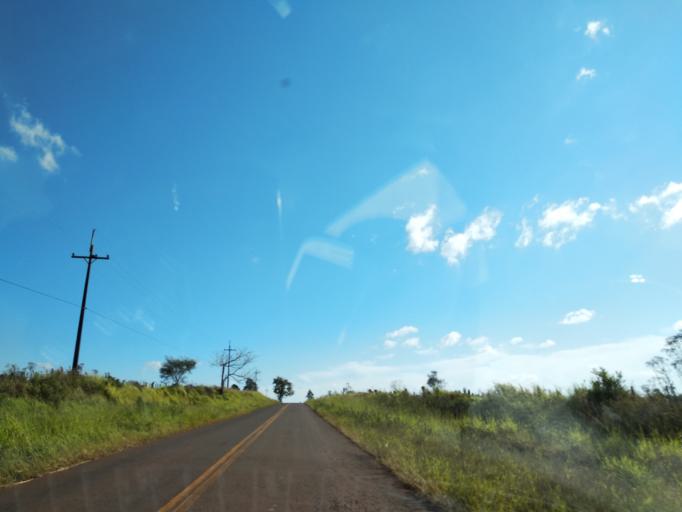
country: PY
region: Itapua
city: Hohenau
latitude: -27.0868
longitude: -55.7013
